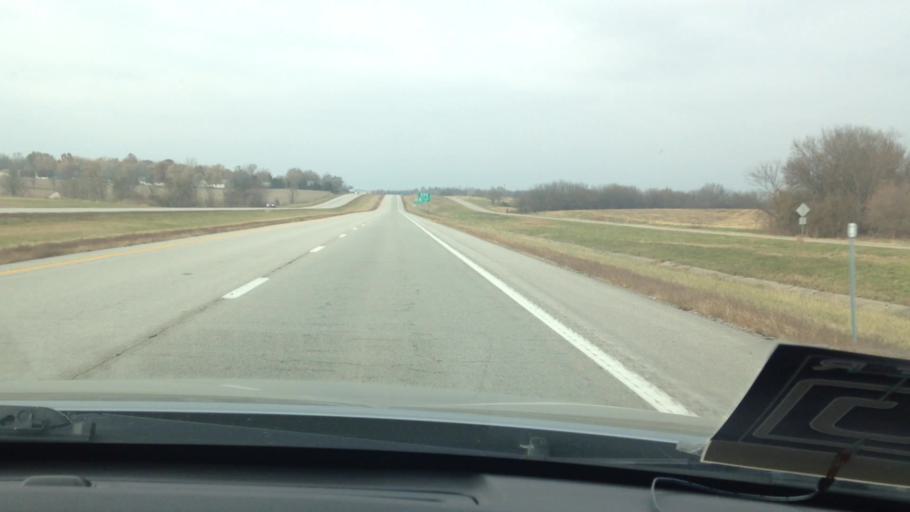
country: US
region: Missouri
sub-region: Cass County
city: Garden City
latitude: 38.5567
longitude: -94.1799
